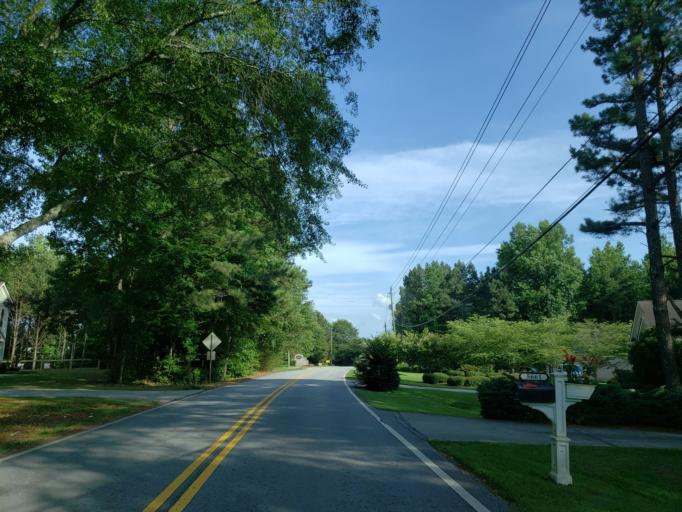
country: US
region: Georgia
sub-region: Paulding County
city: Hiram
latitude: 33.9157
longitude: -84.7182
